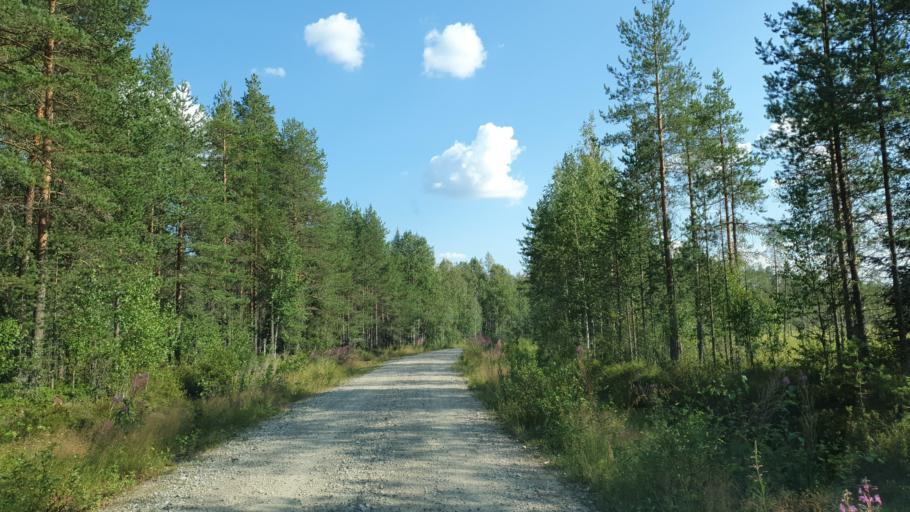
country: FI
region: Kainuu
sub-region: Kehys-Kainuu
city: Kuhmo
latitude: 63.9627
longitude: 29.5527
